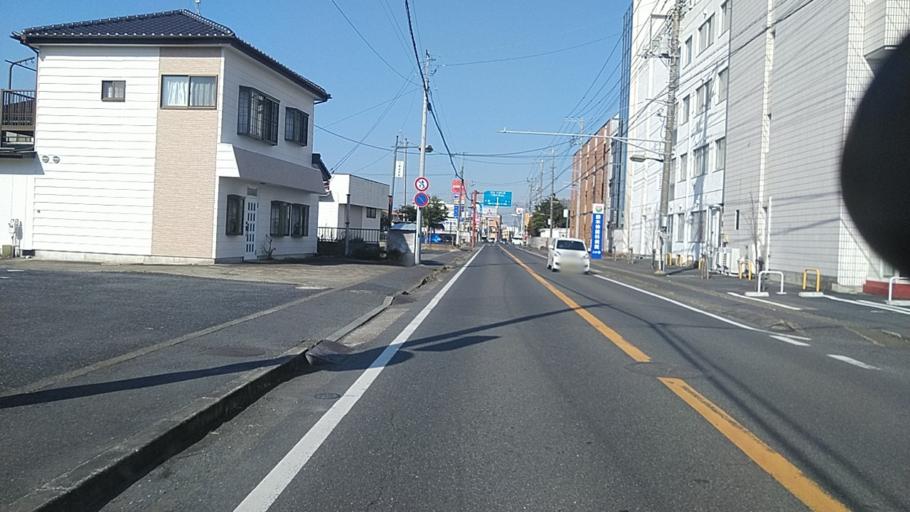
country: JP
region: Chiba
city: Mobara
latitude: 35.4313
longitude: 140.2936
